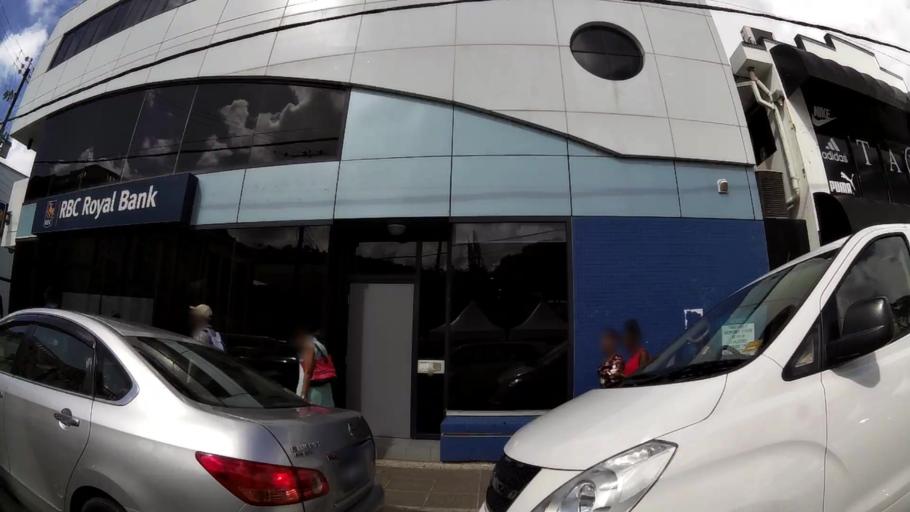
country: LC
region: Castries Quarter
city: Castries
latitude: 14.0093
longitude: -60.9910
